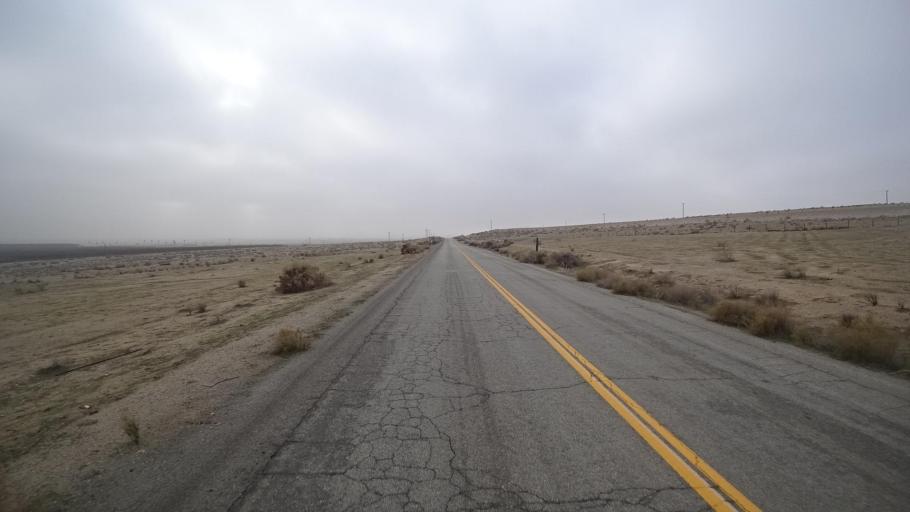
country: US
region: California
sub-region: Kern County
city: Maricopa
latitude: 35.1333
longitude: -119.3551
